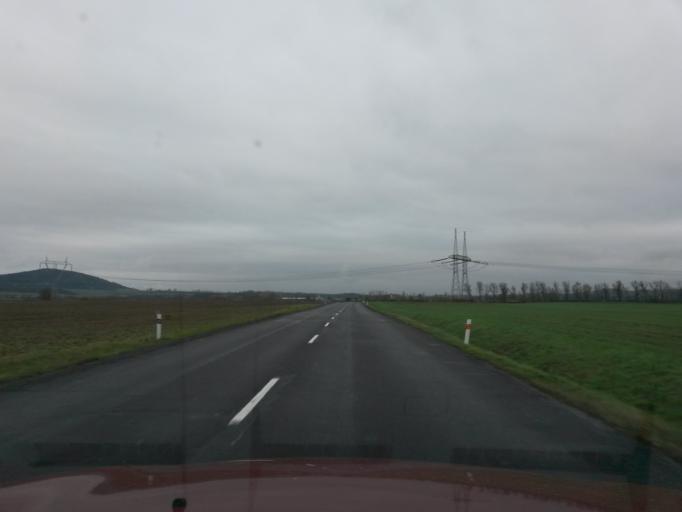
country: SK
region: Kosicky
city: Trebisov
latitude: 48.5118
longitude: 21.7645
